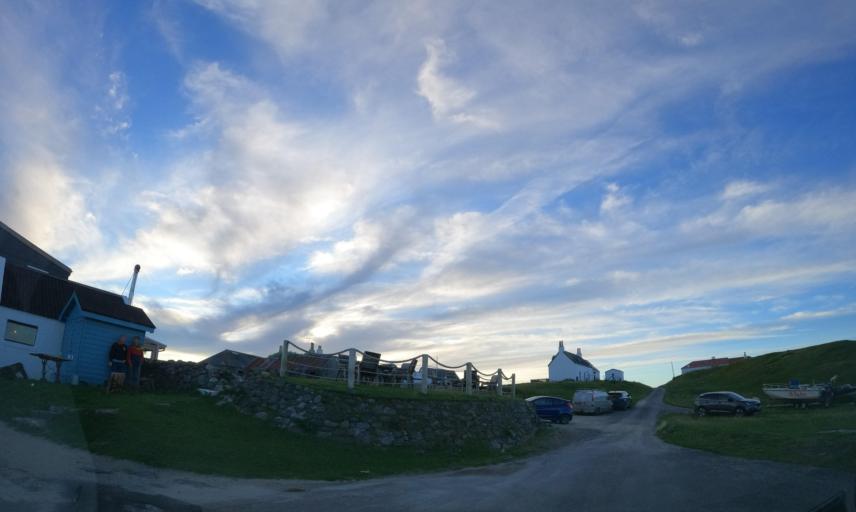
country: GB
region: Scotland
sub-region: Eilean Siar
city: Barra
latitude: 56.5017
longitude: -6.8061
